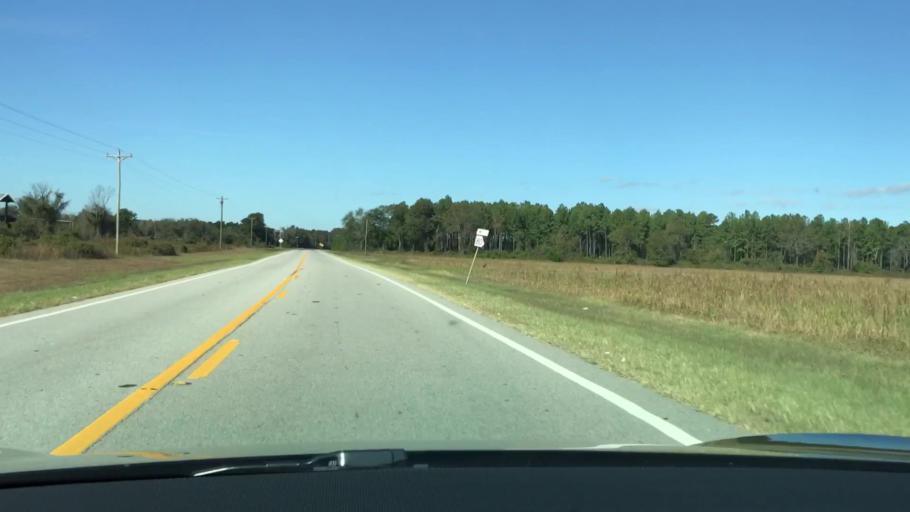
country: US
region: Georgia
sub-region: Glascock County
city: Gibson
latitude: 33.3055
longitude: -82.5257
